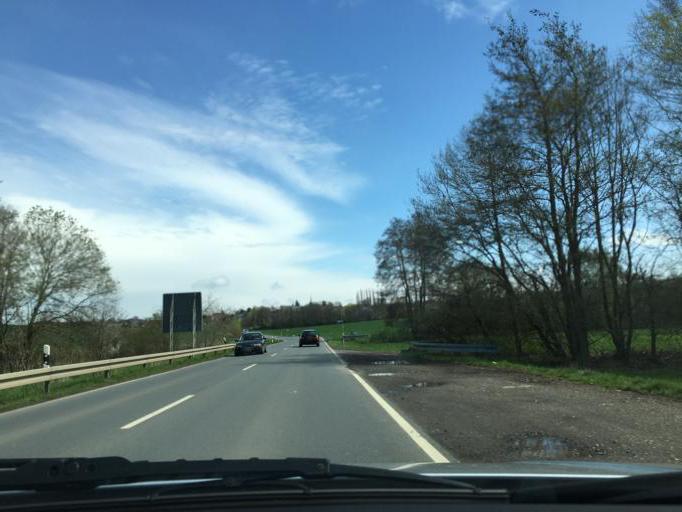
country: DE
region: Hesse
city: Reinheim
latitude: 49.8340
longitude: 8.8863
